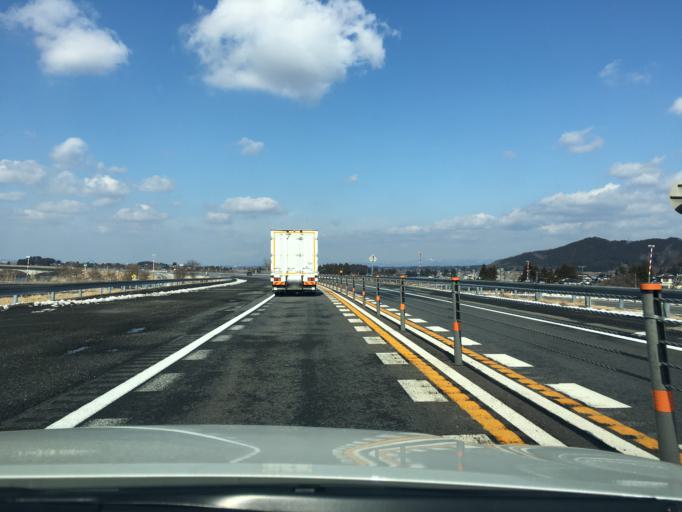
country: JP
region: Yamagata
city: Tsuruoka
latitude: 38.6164
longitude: 139.8431
